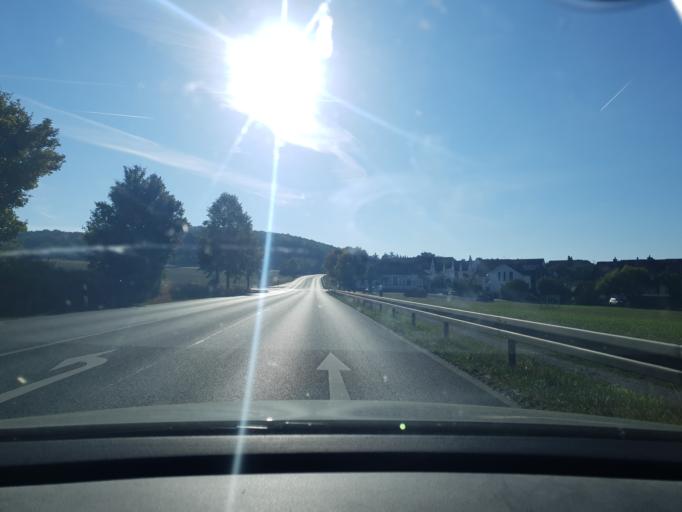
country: DE
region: Hesse
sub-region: Regierungsbezirk Giessen
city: Hoernsheim
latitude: 50.4789
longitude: 8.6163
